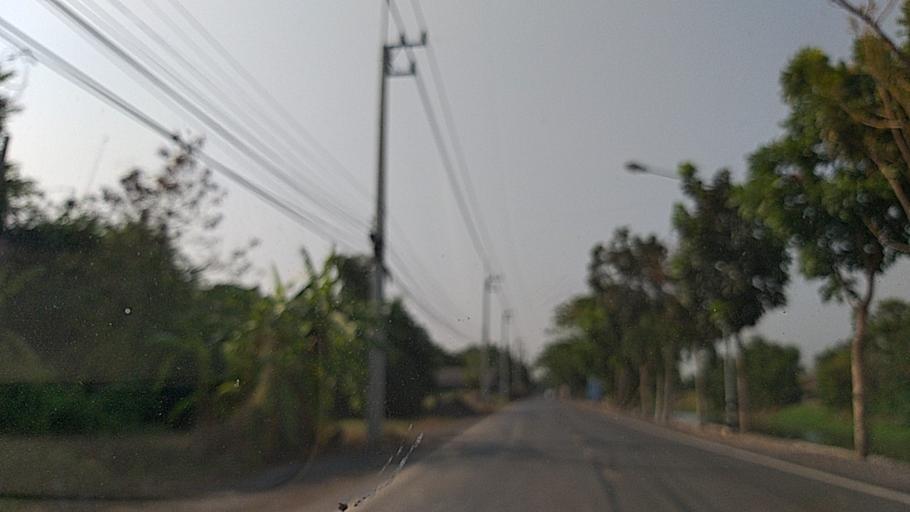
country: TH
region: Pathum Thani
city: Thanyaburi
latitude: 13.9770
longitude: 100.7060
